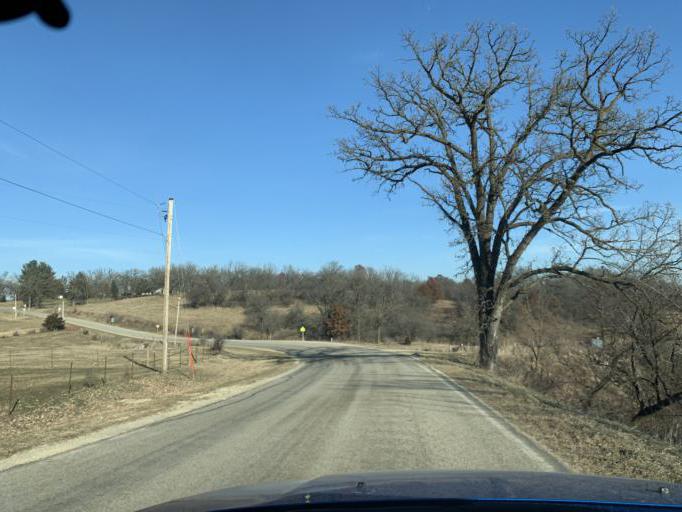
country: US
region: Wisconsin
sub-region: Iowa County
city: Barneveld
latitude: 42.8678
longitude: -89.9328
